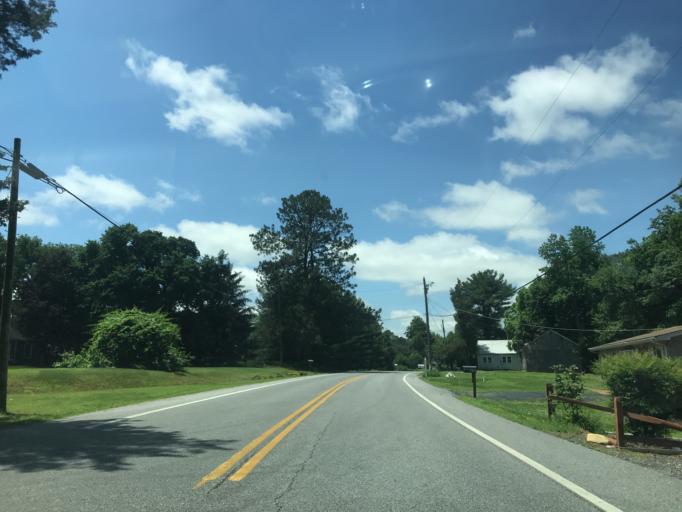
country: US
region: Maryland
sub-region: Caroline County
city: Federalsburg
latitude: 38.6966
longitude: -75.7440
